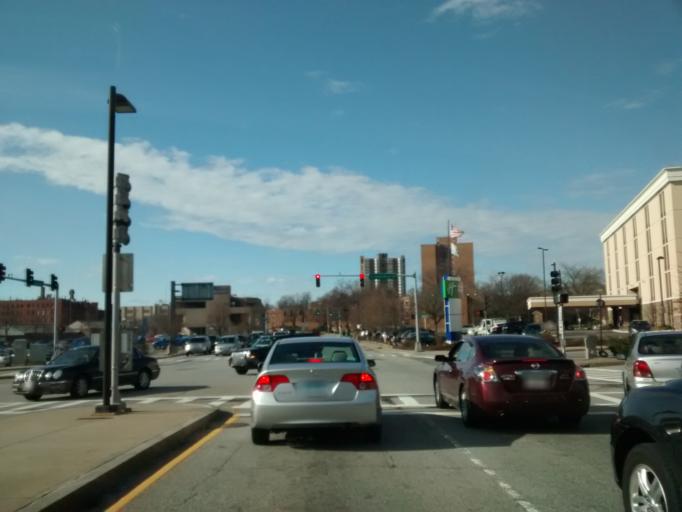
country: US
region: Massachusetts
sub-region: Worcester County
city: Worcester
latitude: 42.2663
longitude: -71.7955
